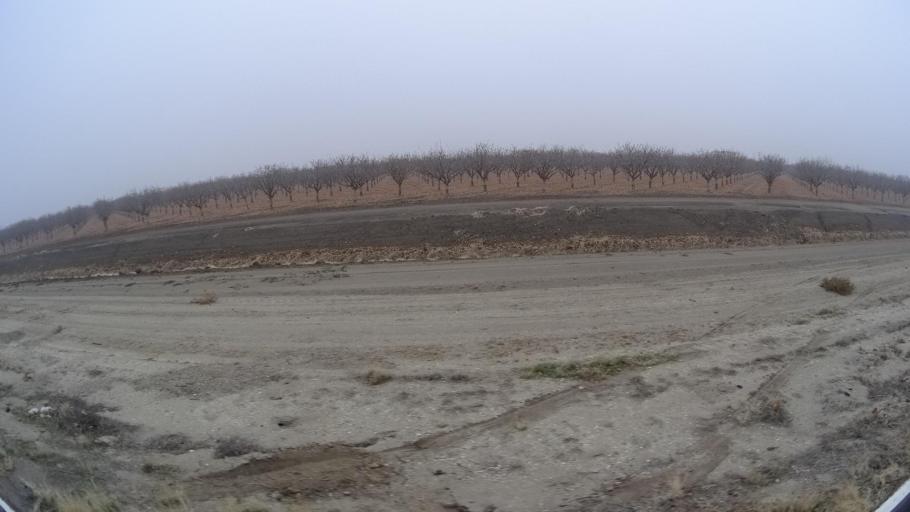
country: US
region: California
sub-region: Kern County
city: Buttonwillow
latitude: 35.4230
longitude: -119.5294
